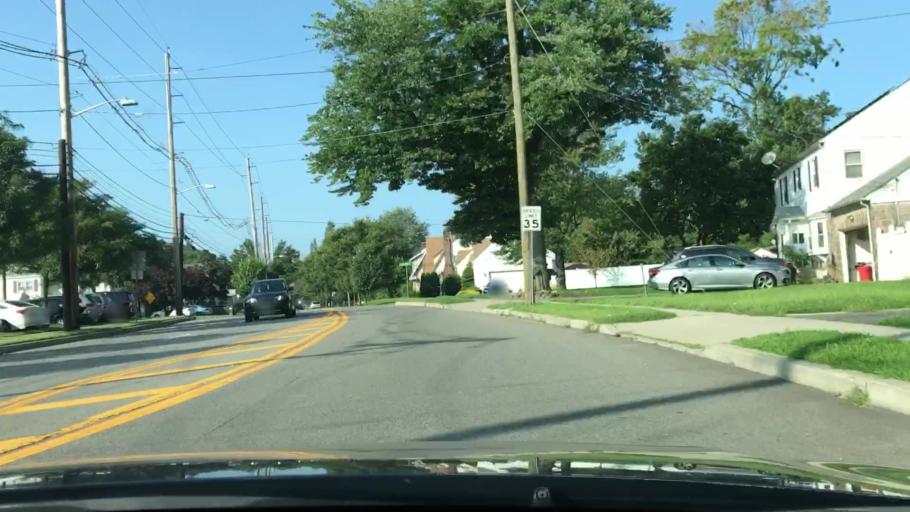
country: US
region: New Jersey
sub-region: Bergen County
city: Maywood
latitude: 40.8897
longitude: -74.0681
